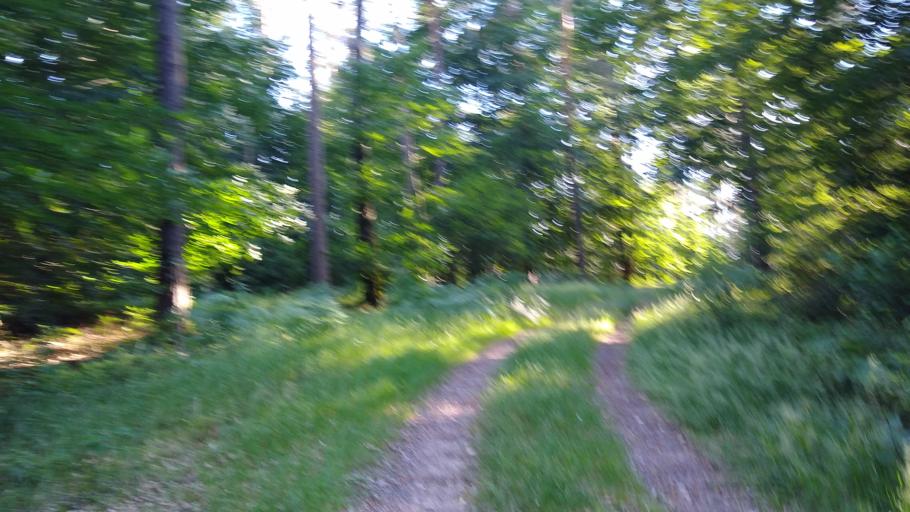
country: DE
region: Hesse
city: Reichelsheim
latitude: 49.6745
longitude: 8.9043
